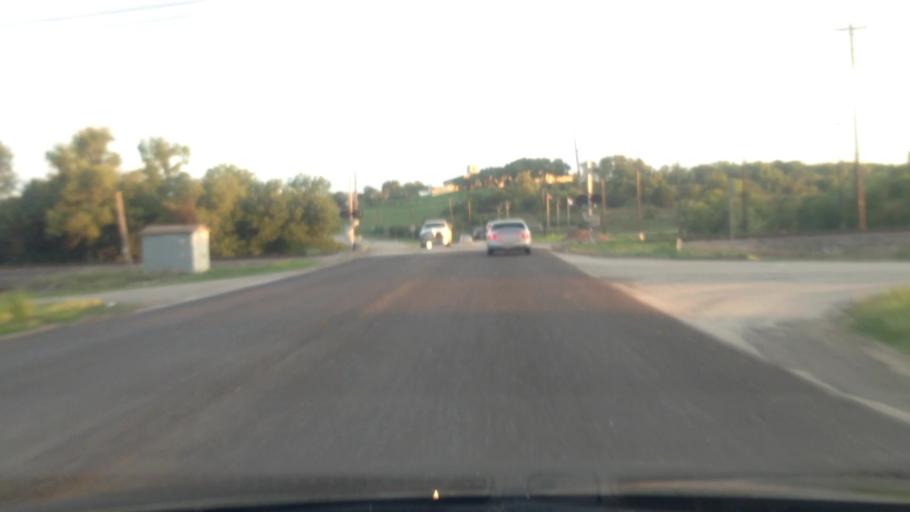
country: US
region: Texas
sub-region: Tarrant County
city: Benbrook
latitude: 32.6788
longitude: -97.4987
